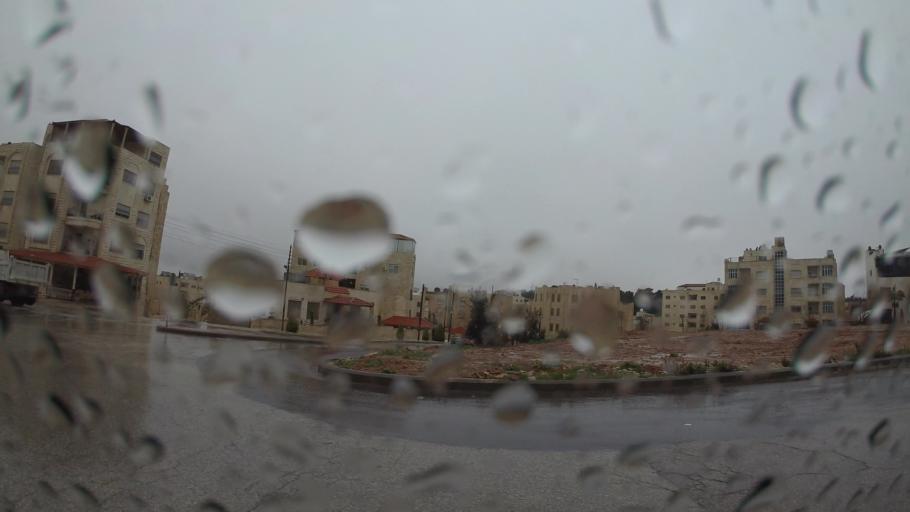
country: JO
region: Amman
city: Al Jubayhah
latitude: 32.0260
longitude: 35.8826
